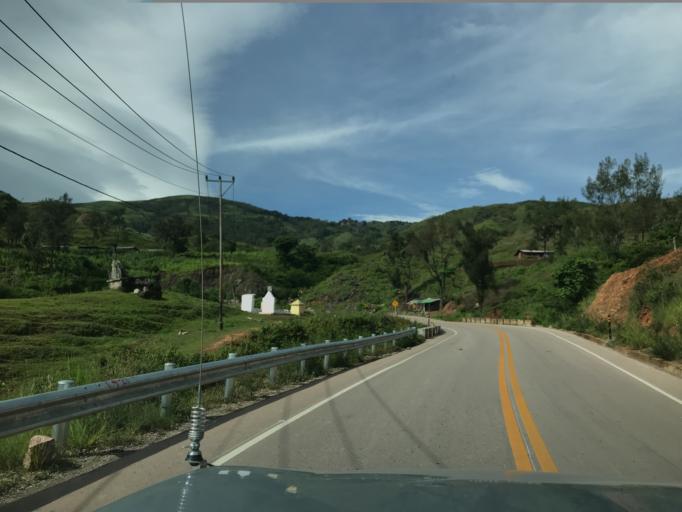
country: TL
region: Aileu
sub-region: Aileu Villa
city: Aileu
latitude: -8.8095
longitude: 125.5971
